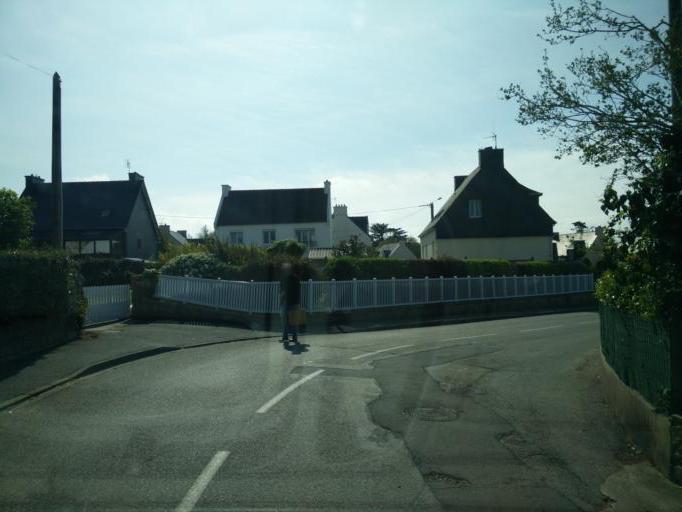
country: FR
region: Brittany
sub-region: Departement du Finistere
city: Crozon
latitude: 48.2434
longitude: -4.4849
